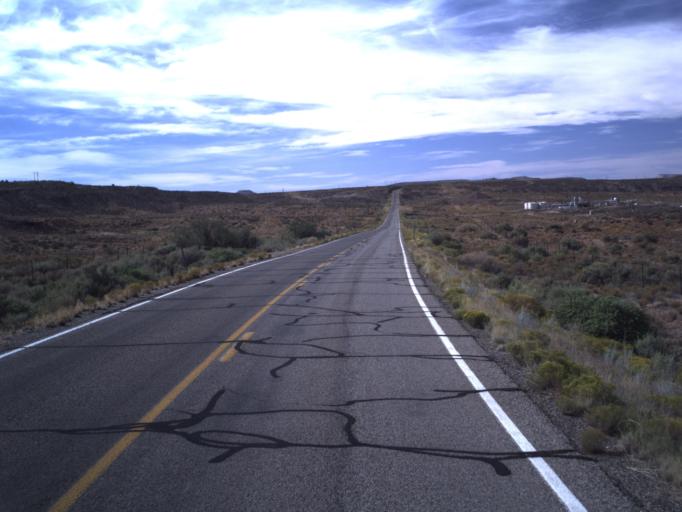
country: US
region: Utah
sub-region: San Juan County
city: Blanding
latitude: 37.3012
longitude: -109.2842
